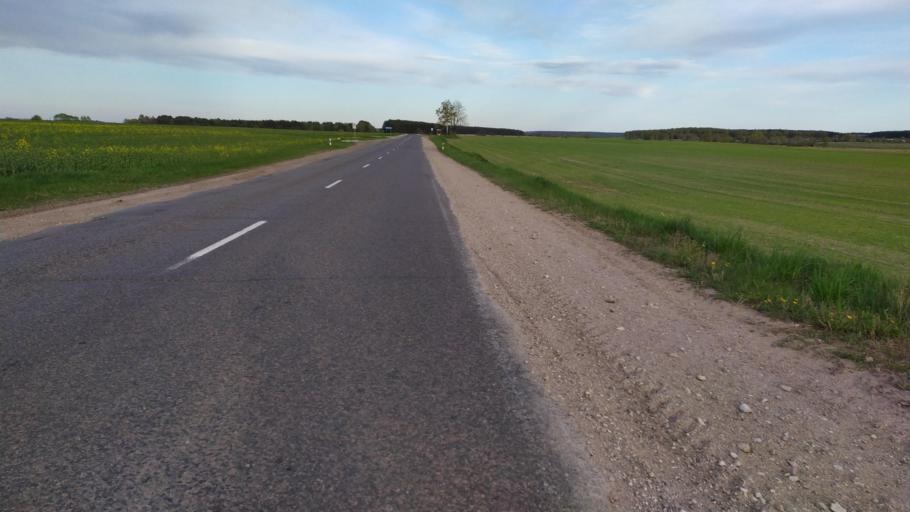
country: BY
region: Brest
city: Kamyanyets
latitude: 52.4121
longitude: 23.7184
